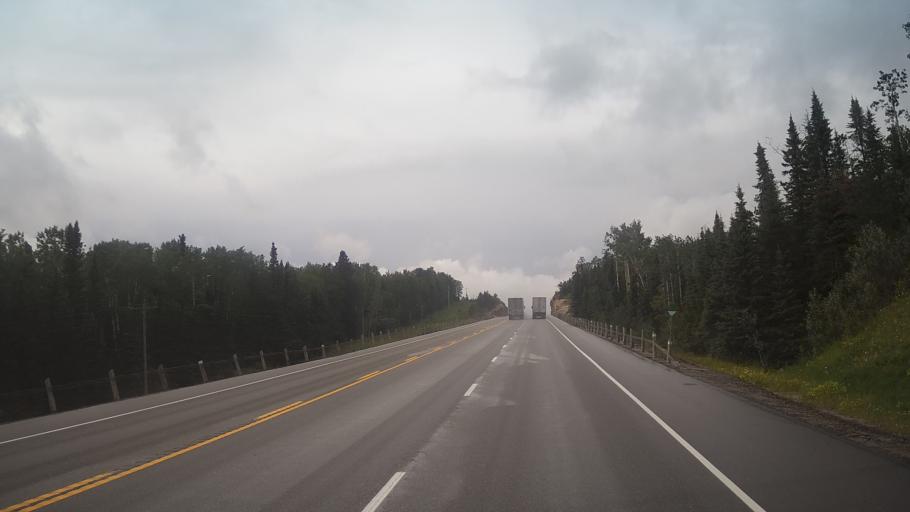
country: CA
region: Ontario
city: Neebing
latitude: 48.6874
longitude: -89.8926
